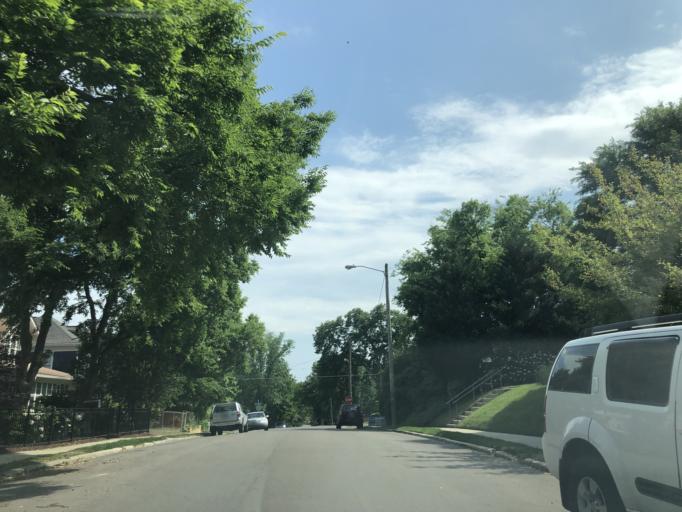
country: US
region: Tennessee
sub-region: Davidson County
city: Nashville
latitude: 36.1267
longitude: -86.7954
